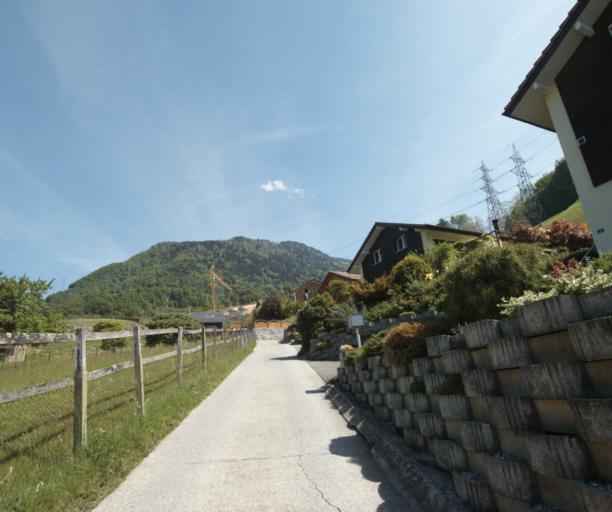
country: CH
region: Vaud
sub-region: Aigle District
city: Villeneuve
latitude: 46.3992
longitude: 6.9387
